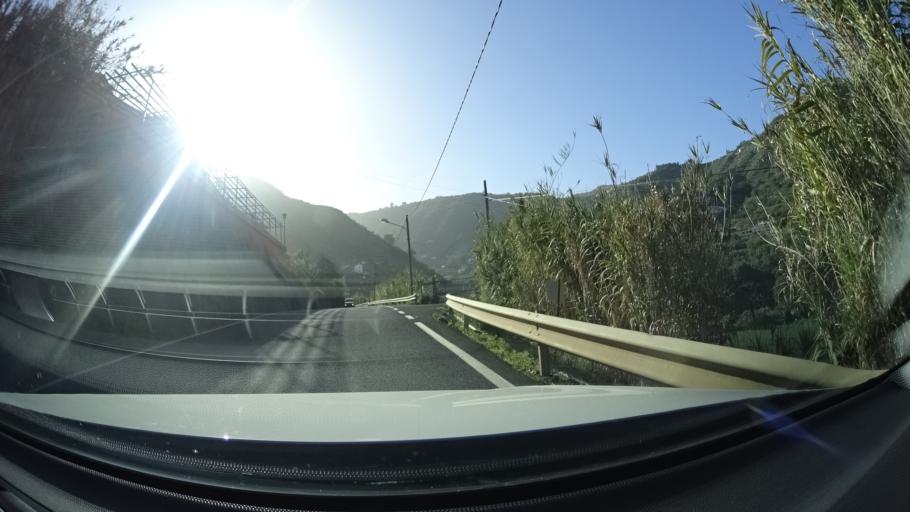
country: ES
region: Canary Islands
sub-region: Provincia de Las Palmas
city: Vega de San Mateo
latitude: 28.0170
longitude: -15.5519
